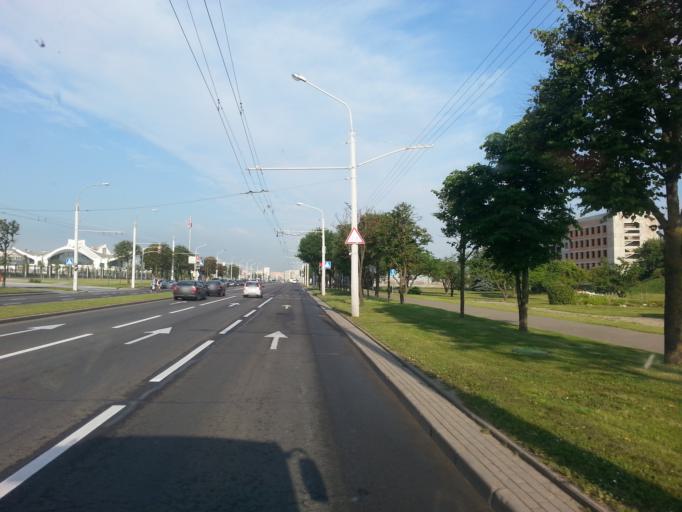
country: BY
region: Minsk
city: Minsk
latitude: 53.9298
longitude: 27.5276
